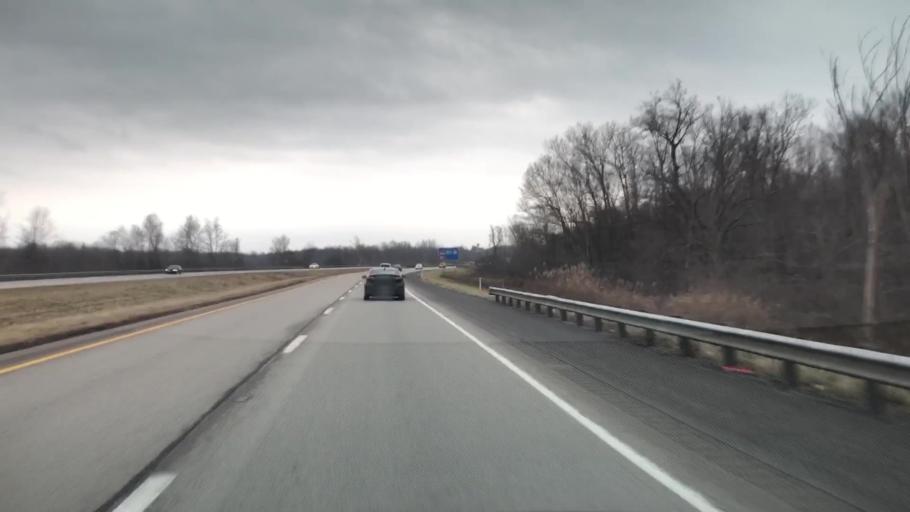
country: US
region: Pennsylvania
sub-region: Mercer County
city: Grove City
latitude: 41.1553
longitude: -80.1575
